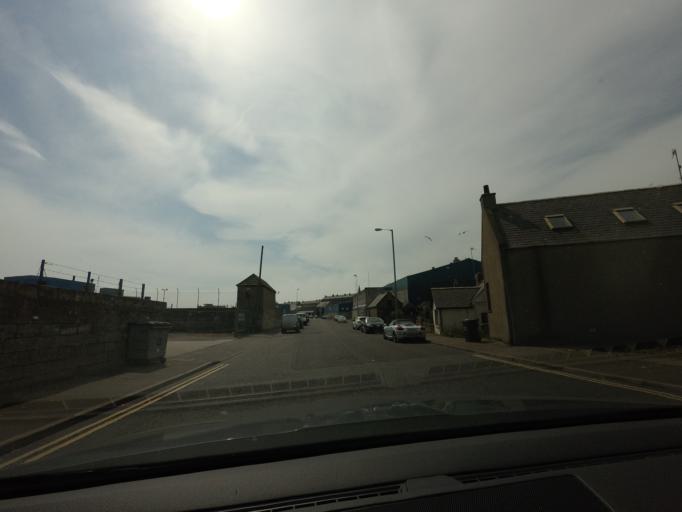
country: GB
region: Scotland
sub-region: Aberdeenshire
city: Peterhead
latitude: 57.5085
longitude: -1.7753
